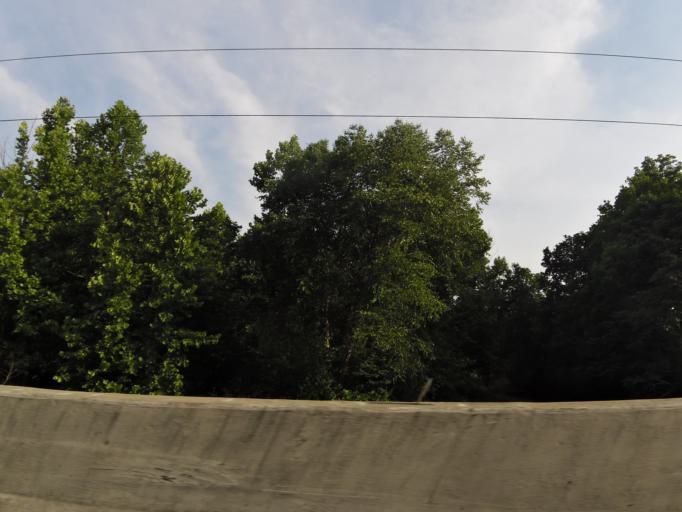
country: US
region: Tennessee
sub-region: Humphreys County
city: McEwen
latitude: 36.0970
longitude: -87.5854
